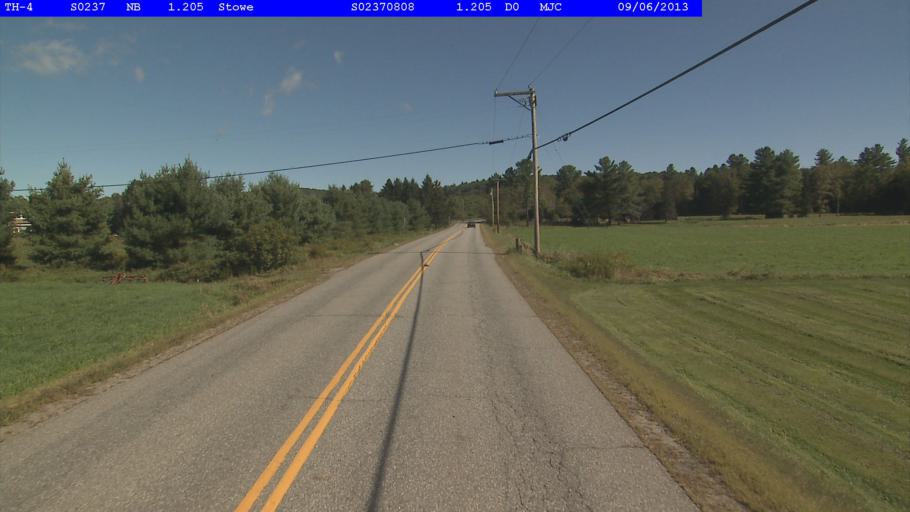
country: US
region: Vermont
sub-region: Lamoille County
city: Morristown
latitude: 44.4980
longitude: -72.6573
